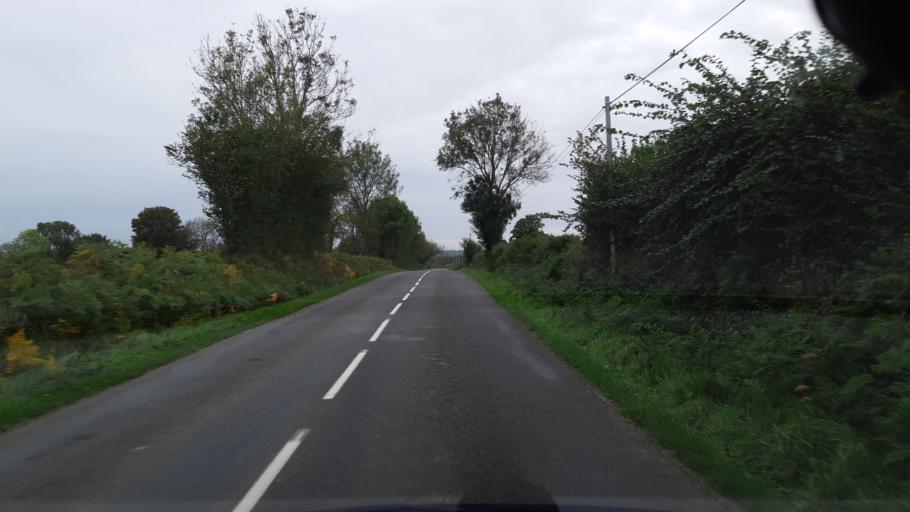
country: FR
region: Lower Normandy
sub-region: Departement de la Manche
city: Hambye
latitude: 48.9651
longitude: -1.2607
